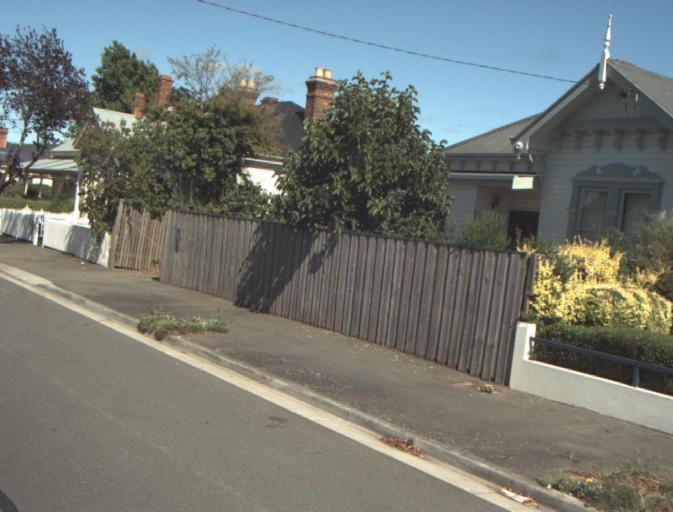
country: AU
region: Tasmania
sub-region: Launceston
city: Newnham
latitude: -41.4156
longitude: 147.1363
